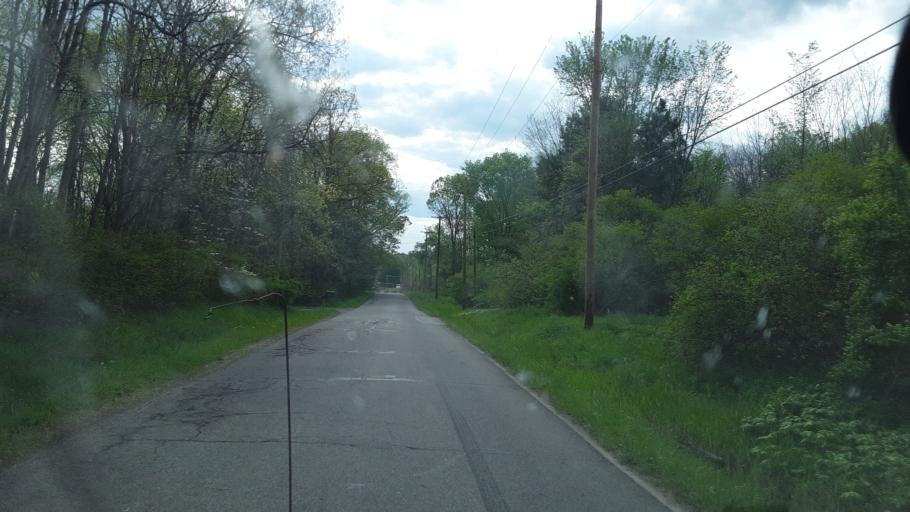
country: US
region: Ohio
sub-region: Portage County
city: Garrettsville
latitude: 41.3478
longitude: -81.0244
